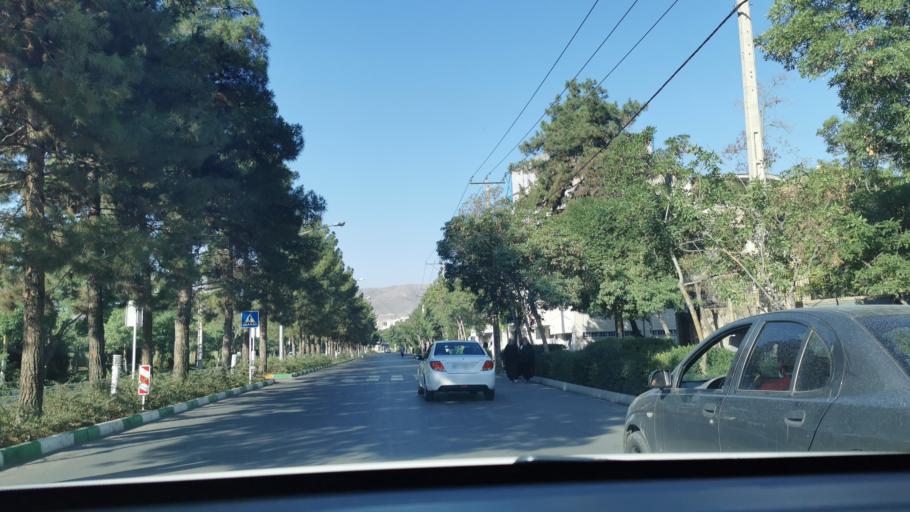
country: IR
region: Razavi Khorasan
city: Mashhad
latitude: 36.3142
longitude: 59.5244
